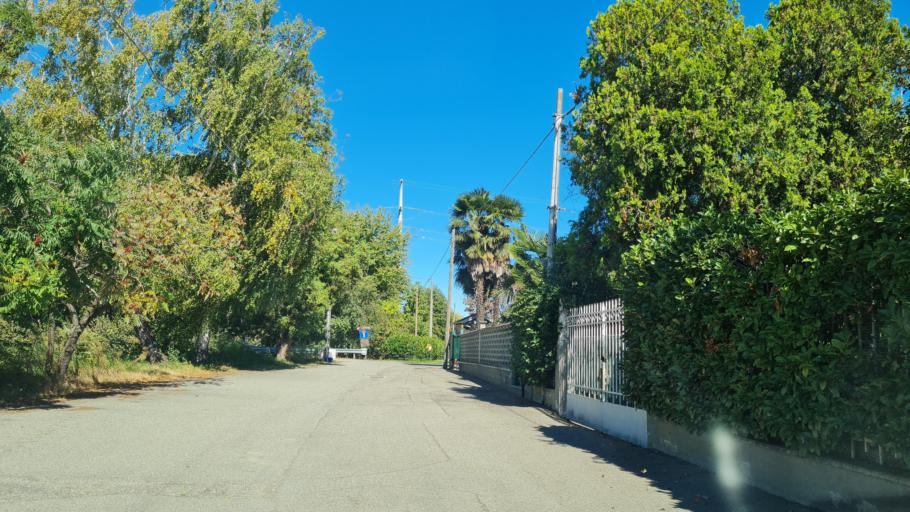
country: IT
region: Piedmont
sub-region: Provincia di Novara
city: Biandrate
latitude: 45.4538
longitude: 8.4585
